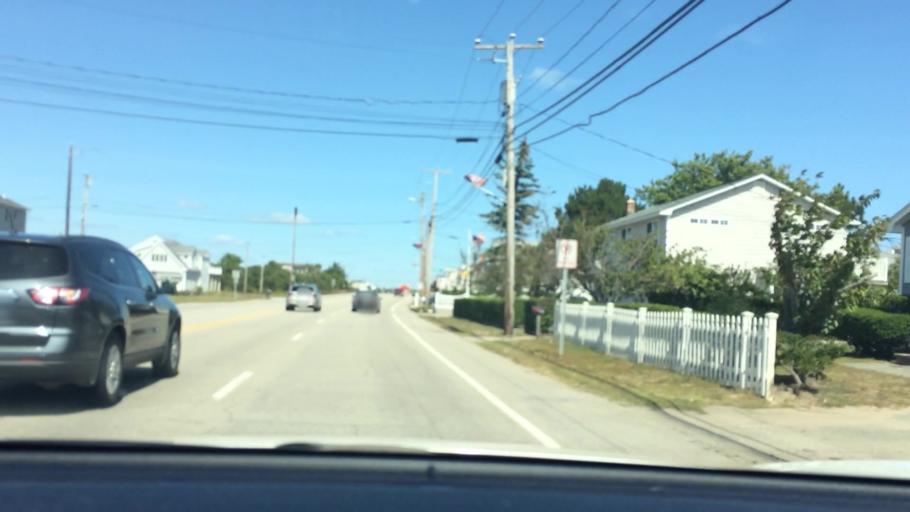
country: US
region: New Hampshire
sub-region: Rockingham County
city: Hampton Beach
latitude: 42.8733
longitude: -70.8183
